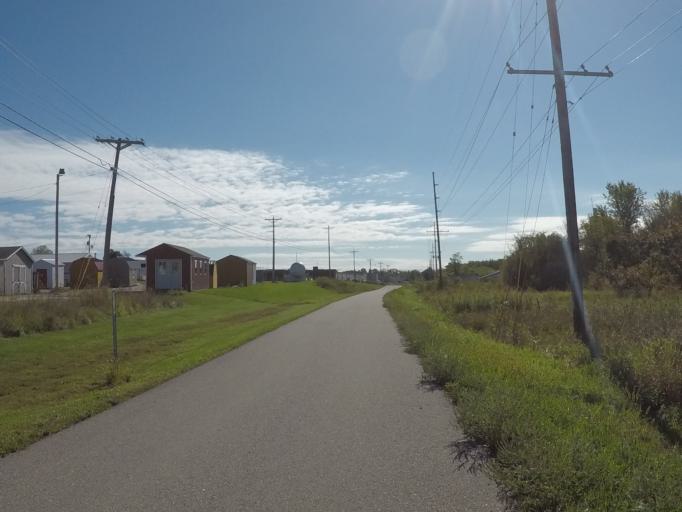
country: US
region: Wisconsin
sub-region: Richland County
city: Richland Center
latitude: 43.3184
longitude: -90.3659
